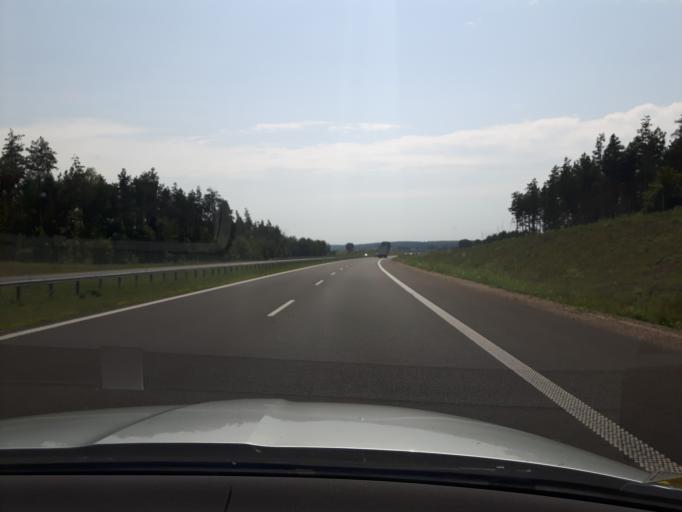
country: PL
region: Masovian Voivodeship
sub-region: Powiat mlawski
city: Wieczfnia Koscielna
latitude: 53.2402
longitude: 20.4236
